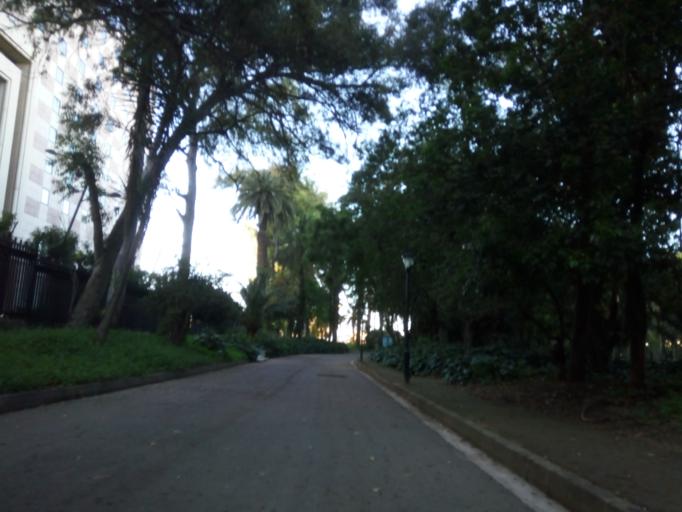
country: DZ
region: Alger
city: Algiers
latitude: 36.7506
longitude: 3.0736
